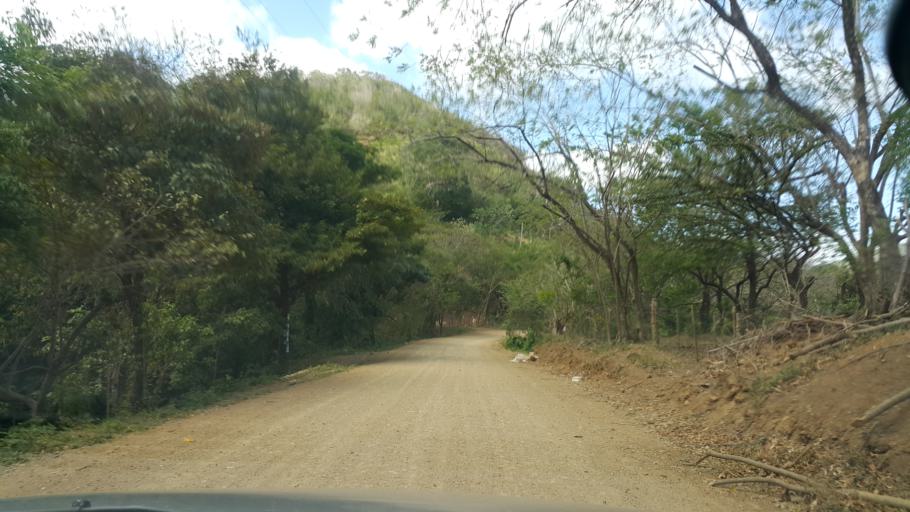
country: NI
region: Rivas
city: San Juan del Sur
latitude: 11.2980
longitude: -85.8679
